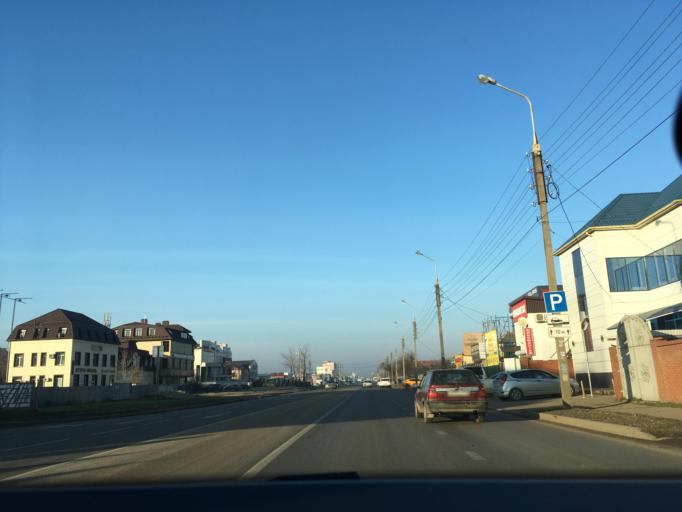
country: RU
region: Krasnodarskiy
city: Krasnodar
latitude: 45.1068
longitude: 39.0127
